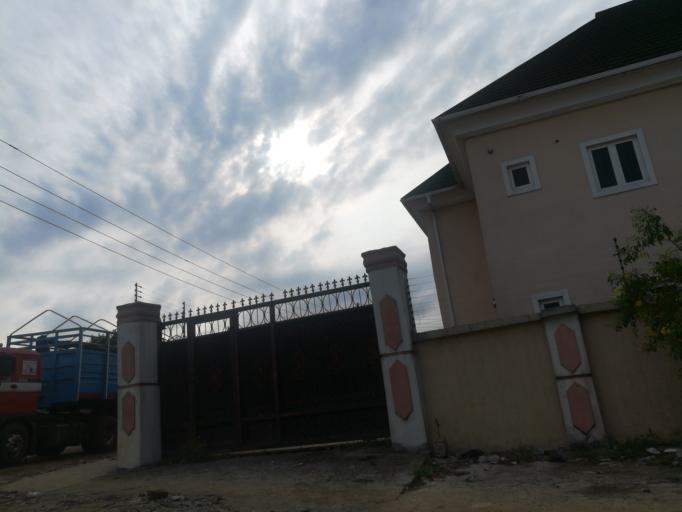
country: NG
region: Rivers
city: Okrika
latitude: 4.7622
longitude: 7.0882
